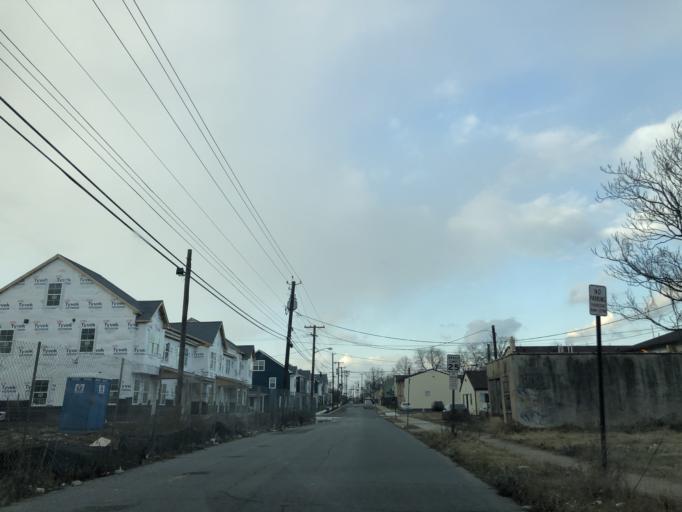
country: US
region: New Jersey
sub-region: Camden County
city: Camden
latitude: 39.9214
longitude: -75.1087
